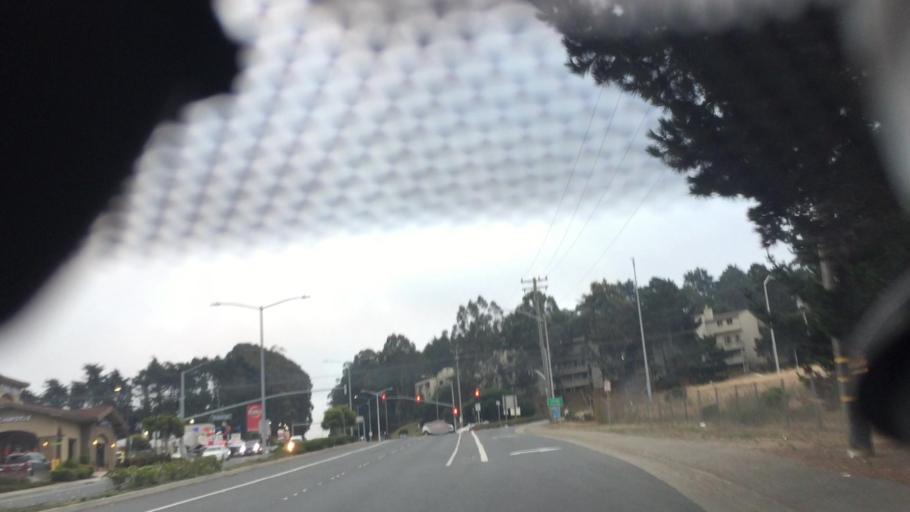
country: US
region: California
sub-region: San Mateo County
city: Colma
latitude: 37.6717
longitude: -122.4655
